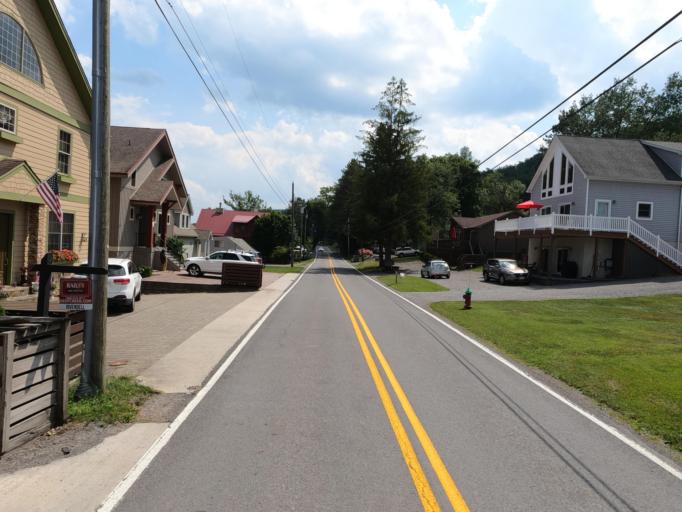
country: US
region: Maryland
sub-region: Garrett County
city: Oakland
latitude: 39.5543
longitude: -79.3592
